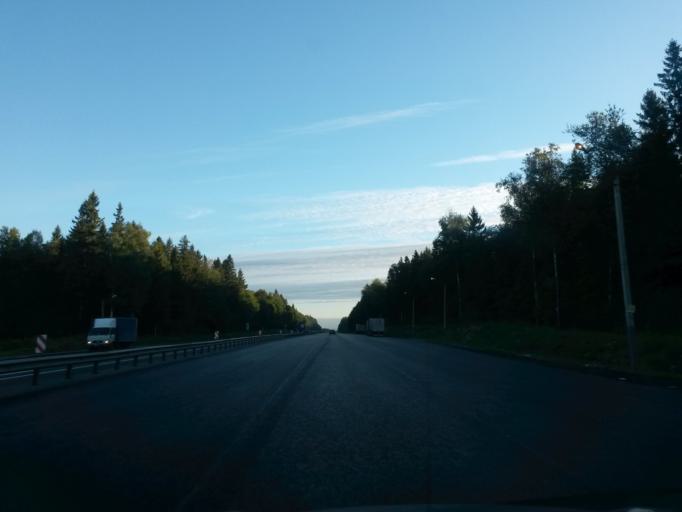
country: RU
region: Moskovskaya
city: Svatkovo
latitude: 56.3924
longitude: 38.3270
